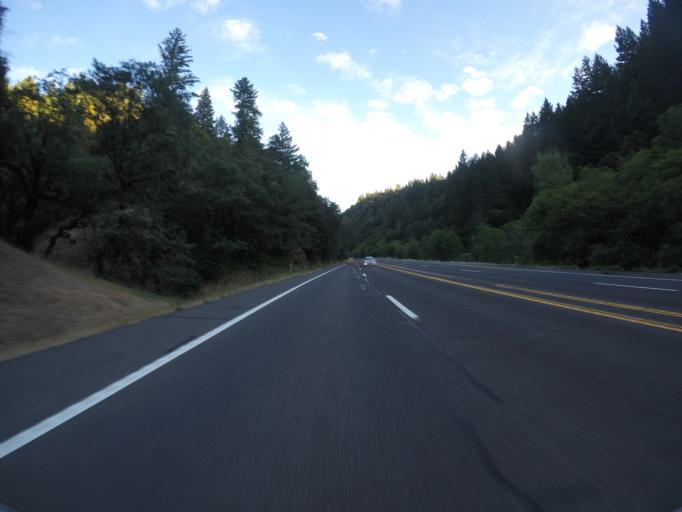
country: US
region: California
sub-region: Mendocino County
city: Laytonville
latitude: 39.5749
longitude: -123.4386
